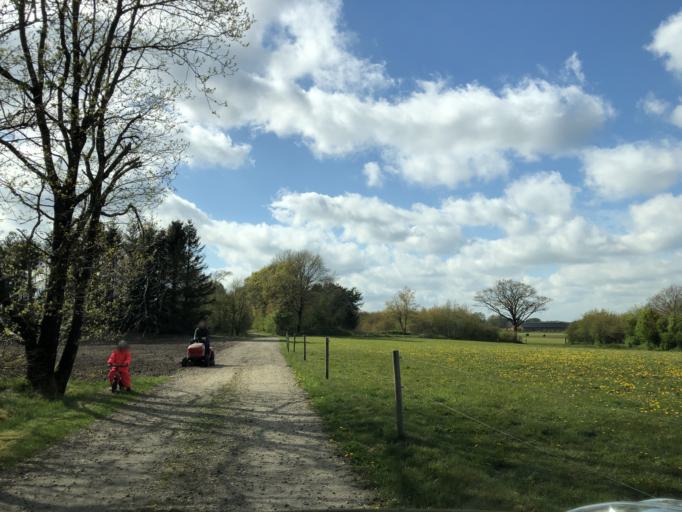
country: DK
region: Central Jutland
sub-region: Herning Kommune
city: Avlum
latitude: 56.2964
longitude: 8.7541
